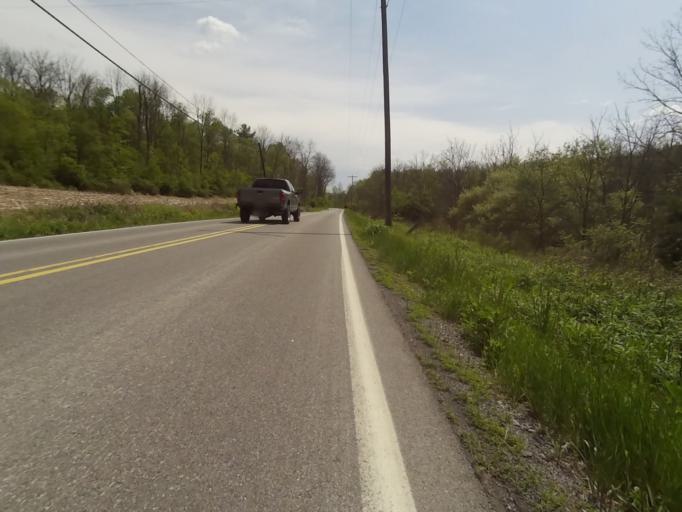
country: US
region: Pennsylvania
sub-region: Centre County
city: Zion
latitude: 40.9923
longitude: -77.6413
